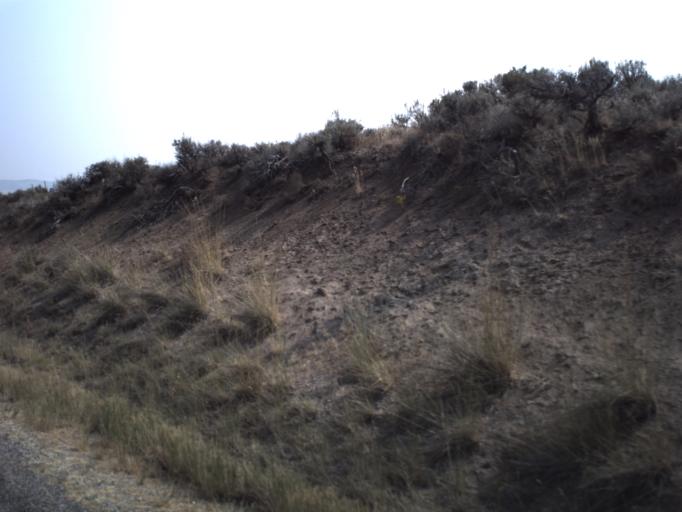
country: US
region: Utah
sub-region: Morgan County
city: Morgan
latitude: 40.9679
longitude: -111.5430
